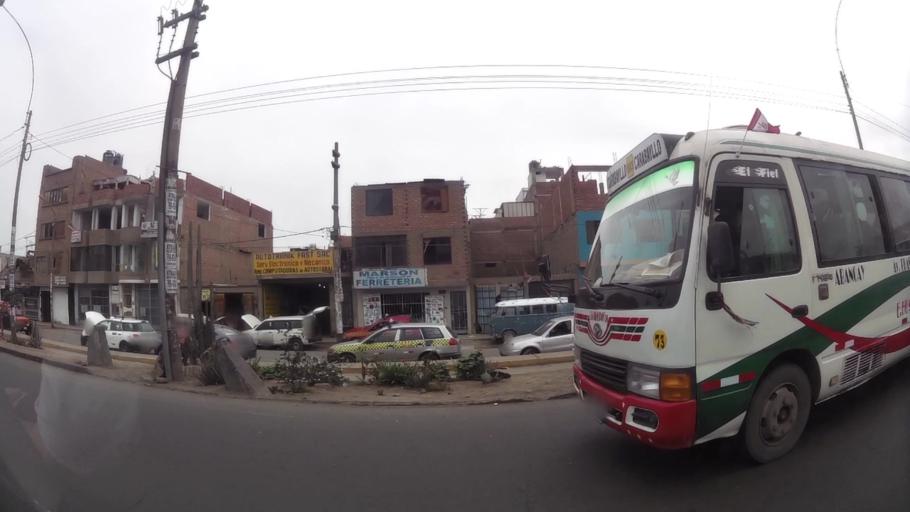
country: PE
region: Lima
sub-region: Lima
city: Independencia
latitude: -12.0107
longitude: -77.0810
